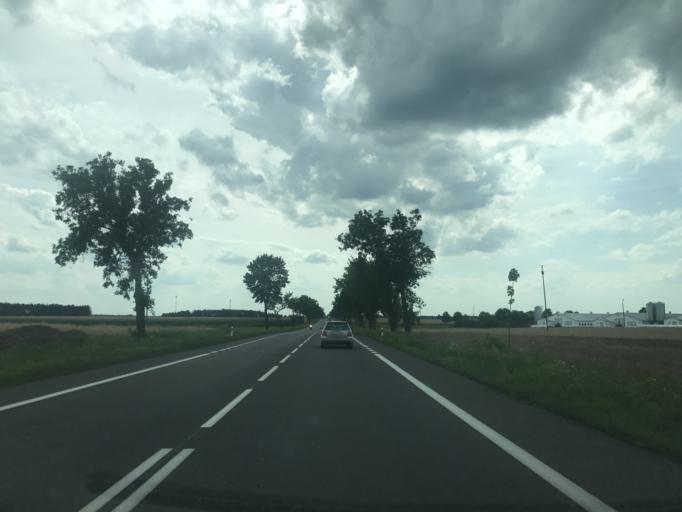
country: PL
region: Masovian Voivodeship
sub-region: Powiat mlawski
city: Strzegowo
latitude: 52.9549
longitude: 20.2956
